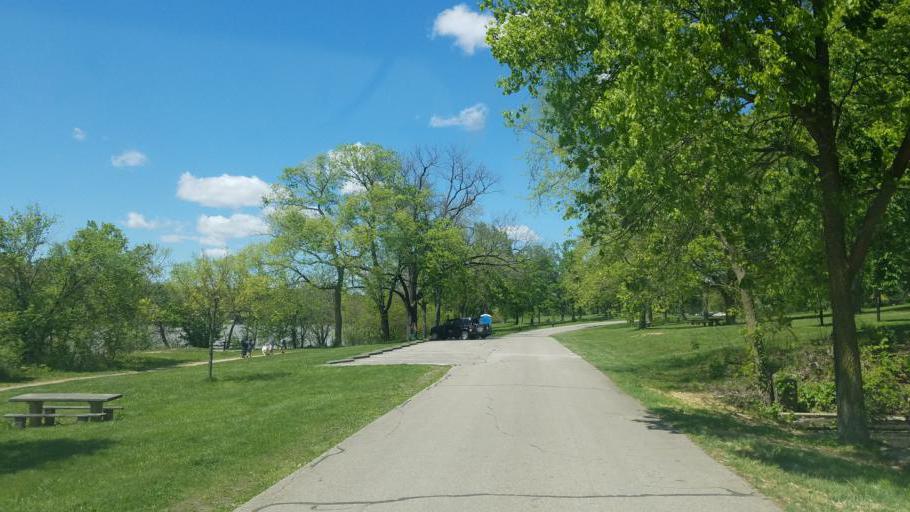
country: US
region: Ohio
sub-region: Franklin County
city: Upper Arlington
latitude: 40.0319
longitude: -83.0934
